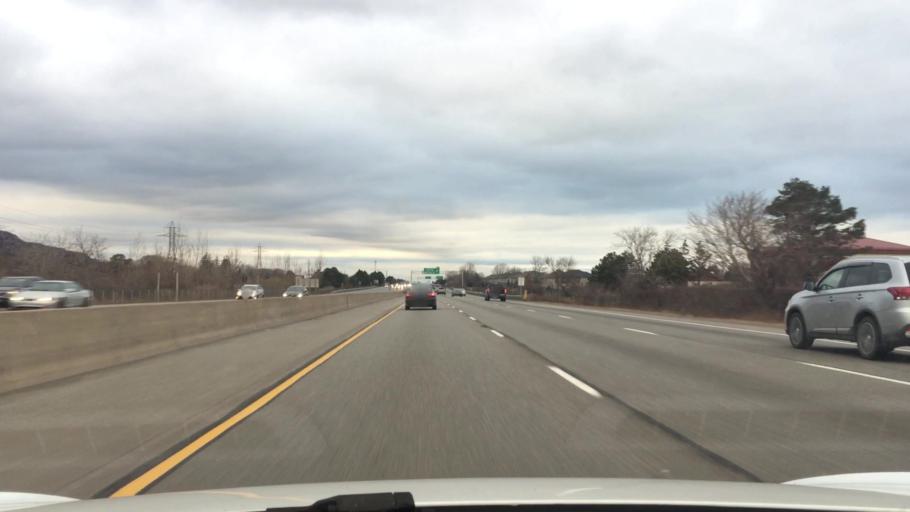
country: CA
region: Ontario
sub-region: Regional Municipality of Niagara
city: St. Catharines
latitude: 43.1928
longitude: -79.5372
